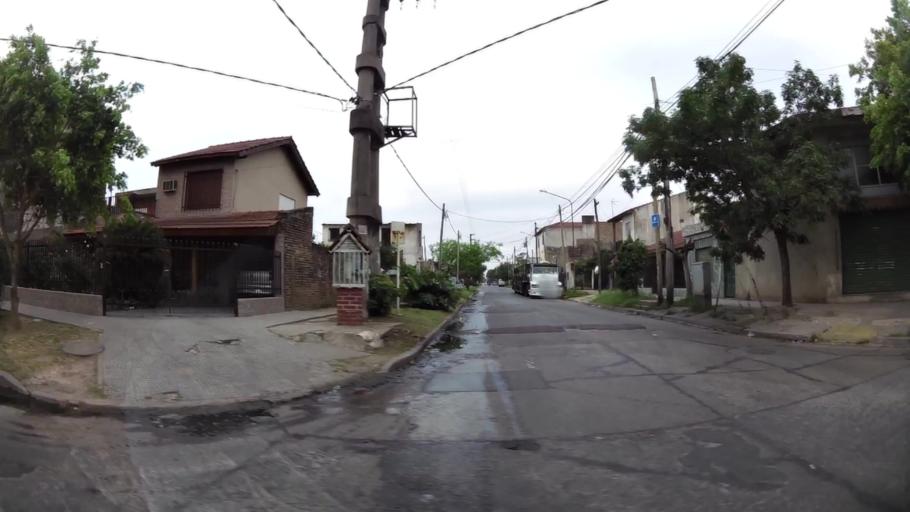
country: AR
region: Buenos Aires
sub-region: Partido de Moron
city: Moron
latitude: -34.6762
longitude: -58.6044
